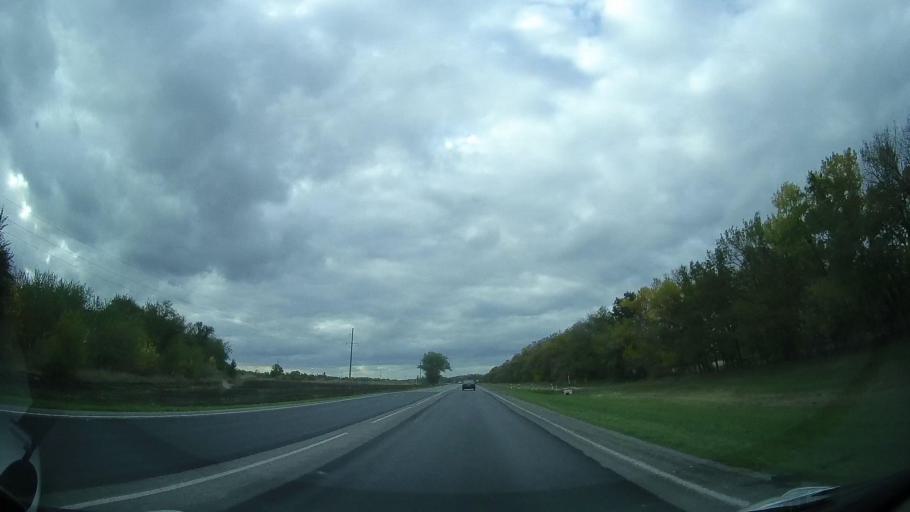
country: RU
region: Rostov
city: Zernograd
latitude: 46.8000
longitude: 40.3631
